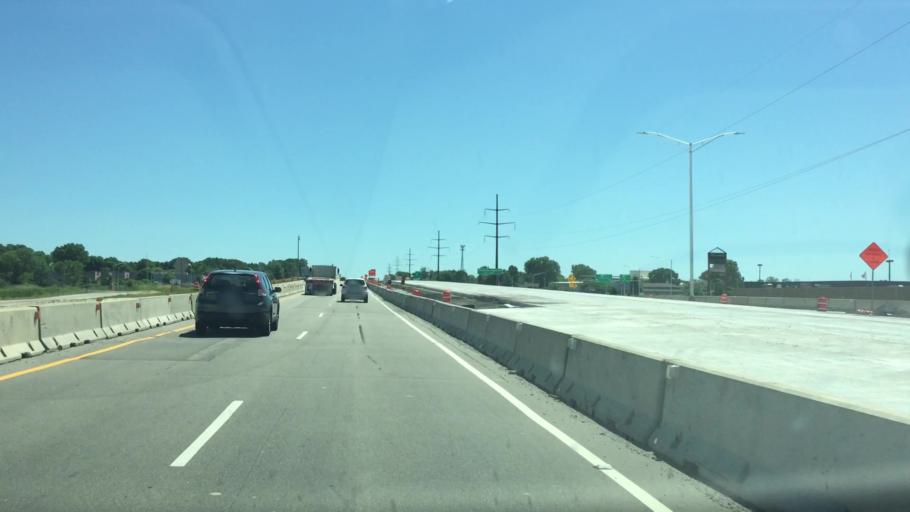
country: US
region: Wisconsin
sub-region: Outagamie County
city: Appleton
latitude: 44.2340
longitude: -88.4286
